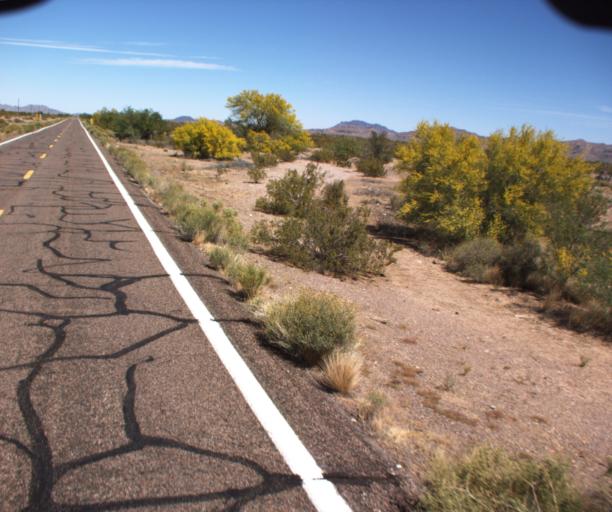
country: US
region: Arizona
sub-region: Pima County
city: Ajo
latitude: 32.6292
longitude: -112.8651
